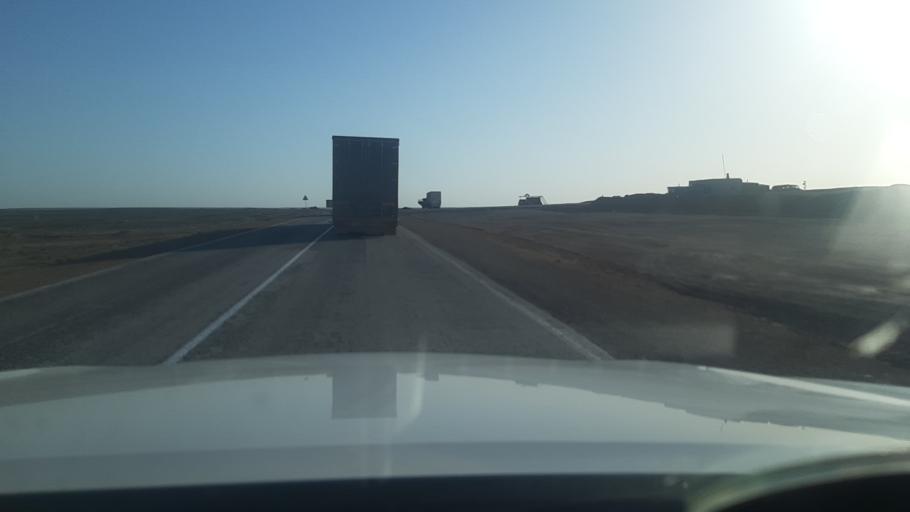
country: KZ
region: Qaraghandy
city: Saryshaghan
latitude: 46.3996
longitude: 73.8715
